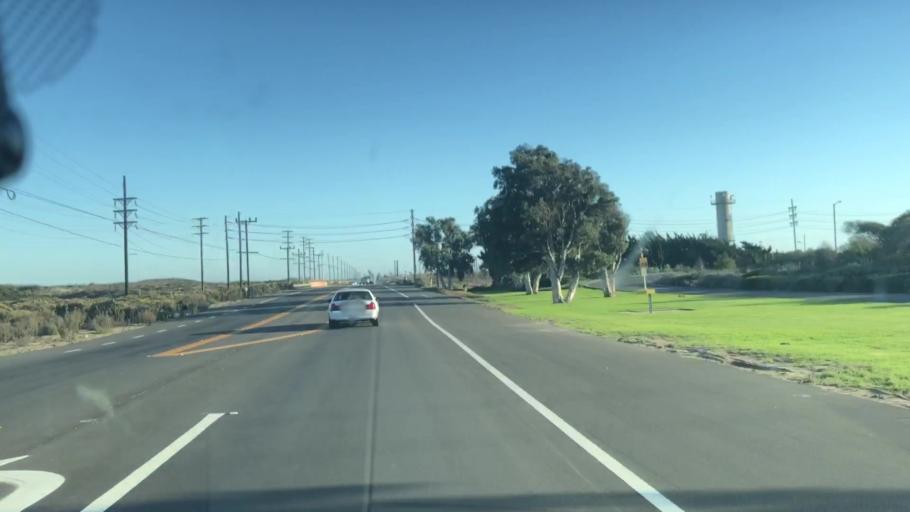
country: US
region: California
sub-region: Ventura County
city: Oxnard Shores
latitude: 34.2079
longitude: -119.2481
